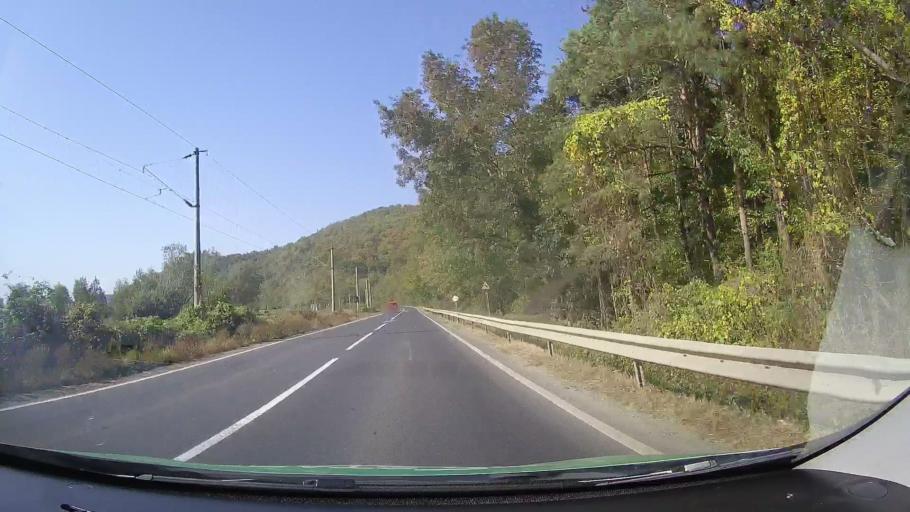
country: RO
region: Arad
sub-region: Oras Lipova
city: Lipova
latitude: 46.1080
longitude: 21.7371
